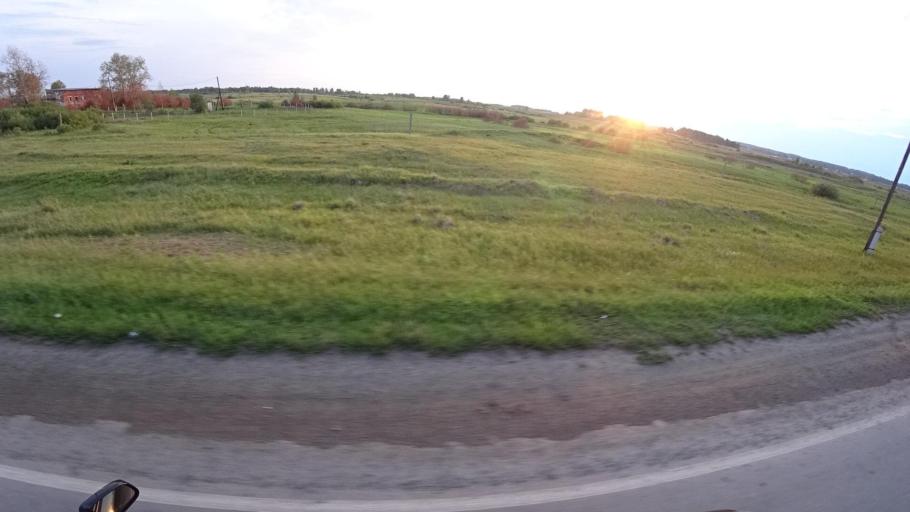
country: RU
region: Sverdlovsk
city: Kamyshlov
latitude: 56.8683
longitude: 62.7108
